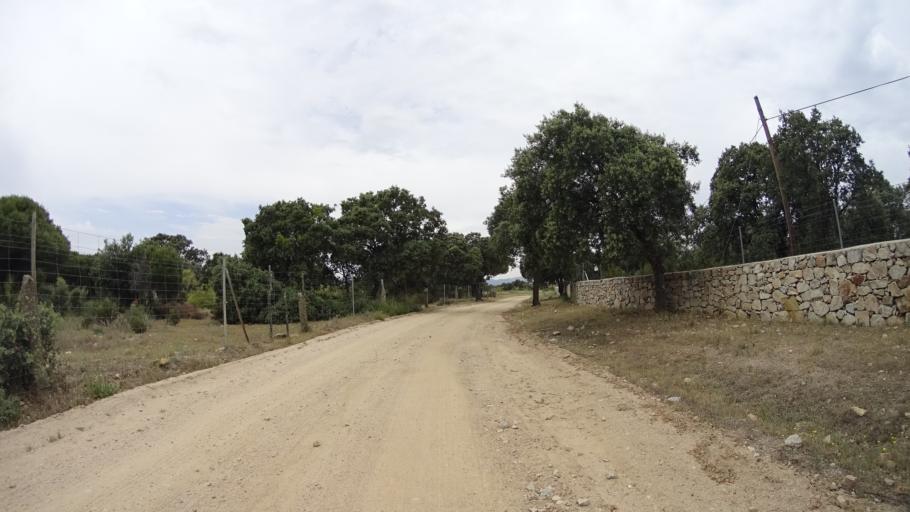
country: ES
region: Madrid
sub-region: Provincia de Madrid
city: Colmenarejo
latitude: 40.5455
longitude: -4.0373
